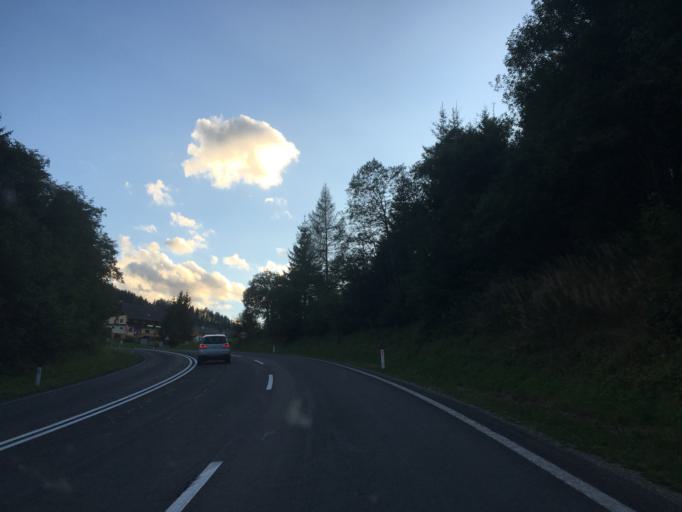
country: AT
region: Styria
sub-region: Politischer Bezirk Murtal
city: Hohentauern
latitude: 47.4345
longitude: 14.4885
